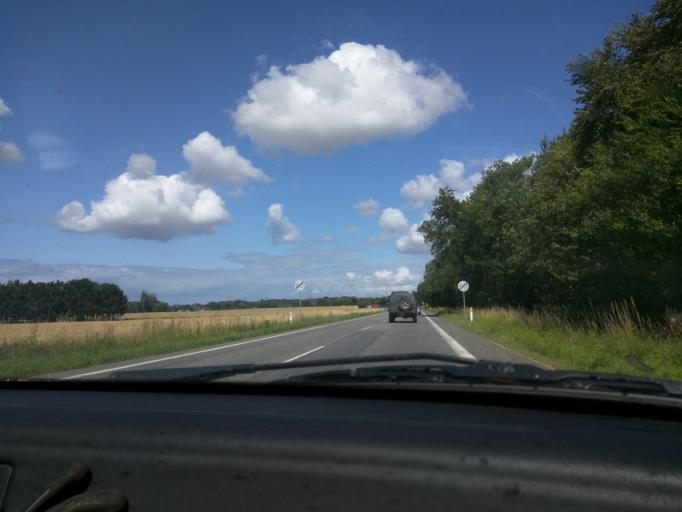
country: DK
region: Zealand
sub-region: Kalundborg Kommune
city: Svebolle
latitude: 55.6664
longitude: 11.2771
